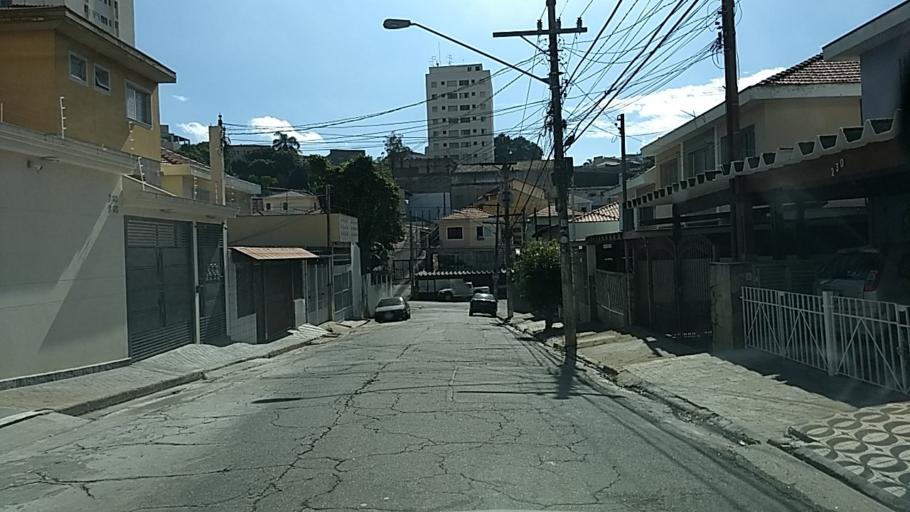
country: BR
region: Sao Paulo
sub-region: Guarulhos
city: Guarulhos
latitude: -23.4805
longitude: -46.5973
